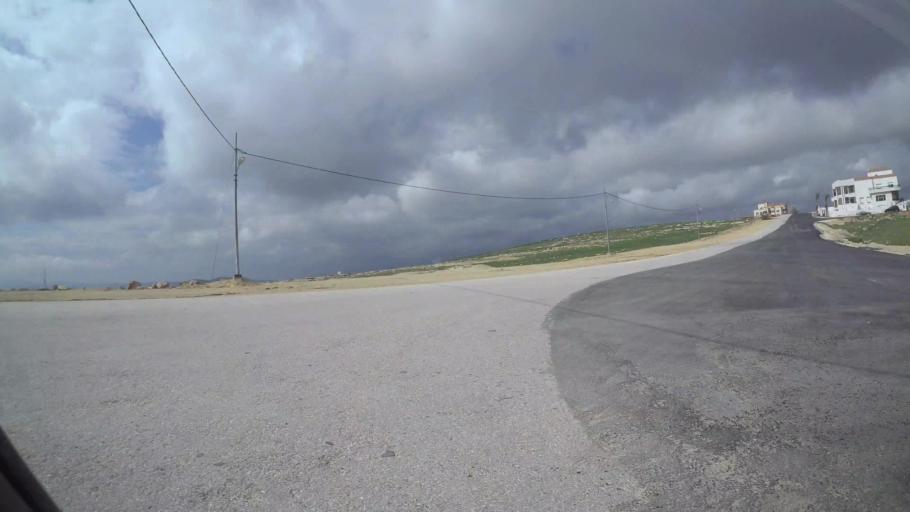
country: JO
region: Amman
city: Al Jubayhah
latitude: 32.0759
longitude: 35.8832
